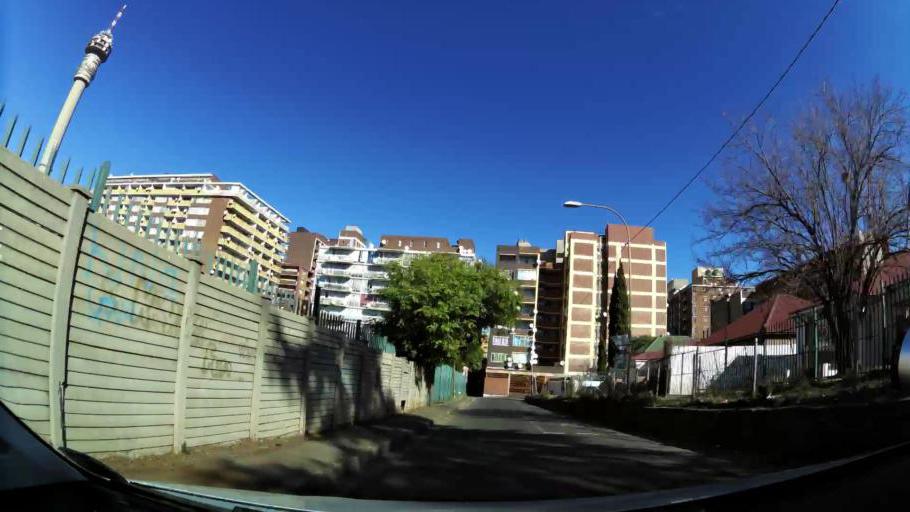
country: ZA
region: Gauteng
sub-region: City of Johannesburg Metropolitan Municipality
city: Johannesburg
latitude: -26.1834
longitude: 28.0503
